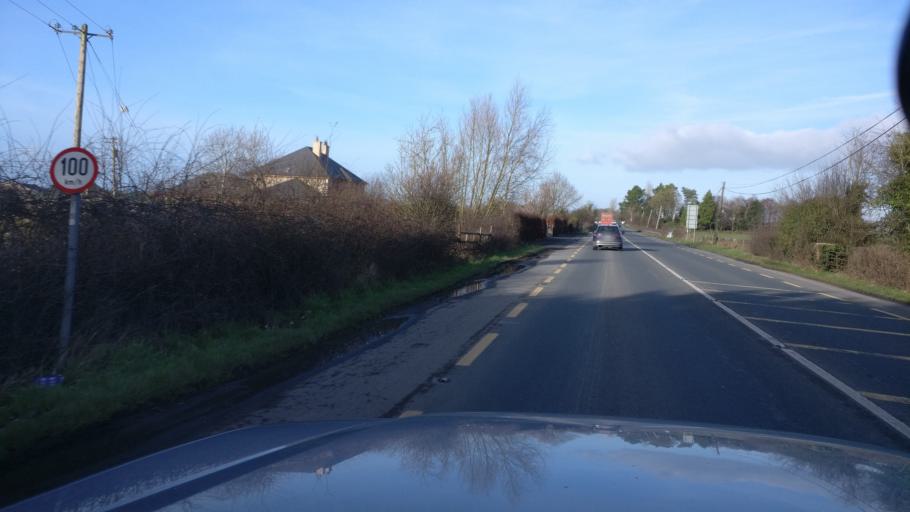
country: IE
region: Leinster
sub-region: Uibh Fhaili
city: Tullamore
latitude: 53.2422
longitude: -7.4780
